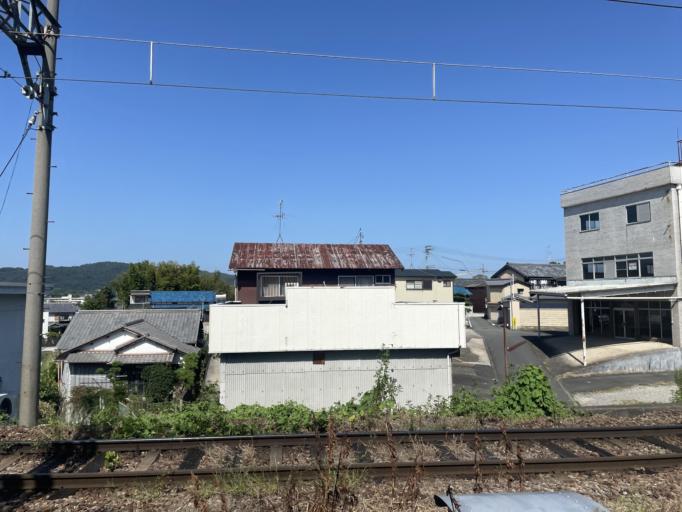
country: JP
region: Nara
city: Tawaramoto
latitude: 34.5892
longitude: 135.7201
